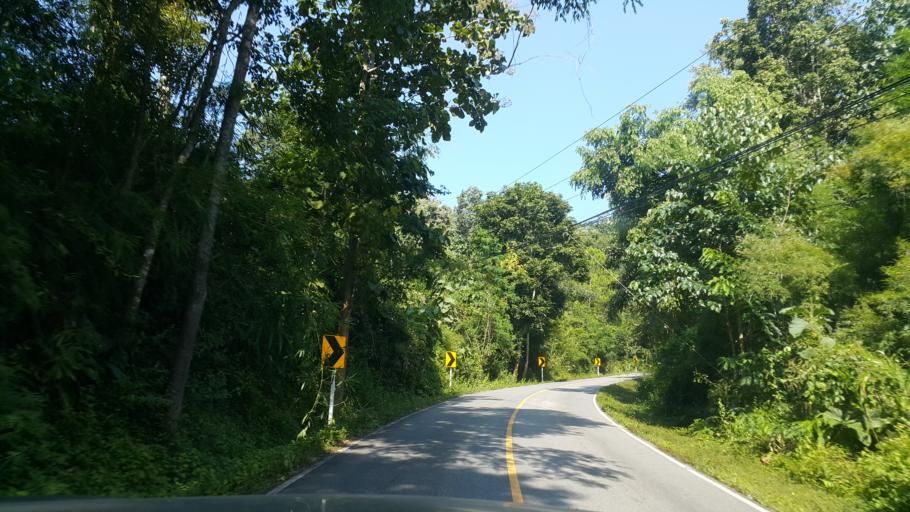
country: TH
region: Chiang Mai
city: Samoeng
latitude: 18.8588
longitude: 98.6541
